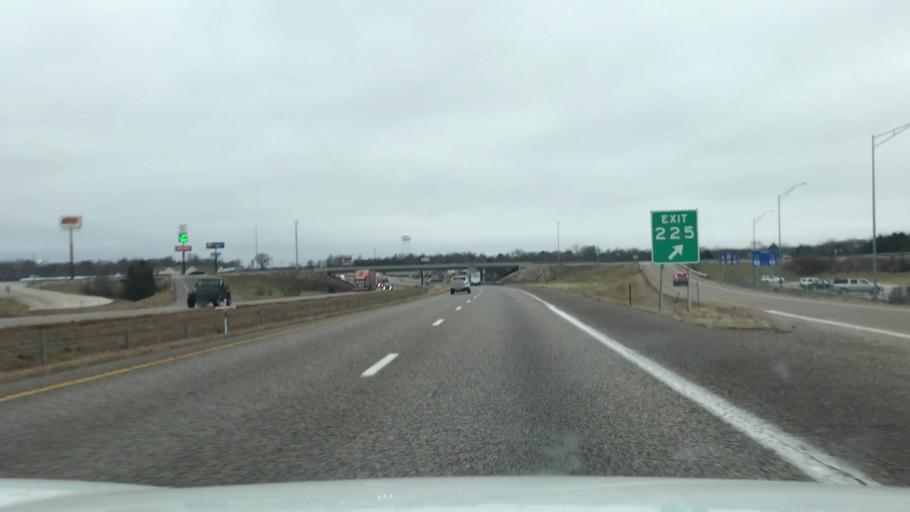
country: US
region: Missouri
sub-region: Franklin County
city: Sullivan
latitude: 38.2136
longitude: -91.1703
